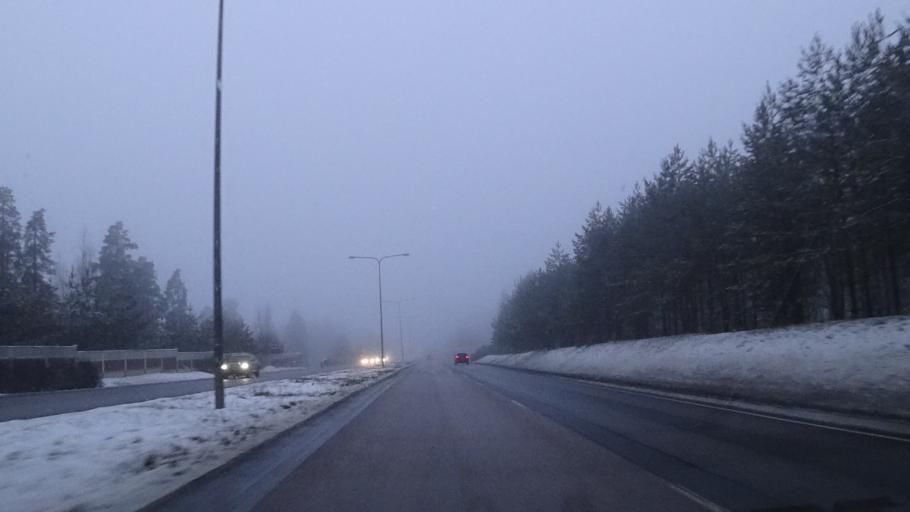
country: FI
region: Paijanne Tavastia
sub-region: Lahti
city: Hollola
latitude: 60.9869
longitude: 25.5292
